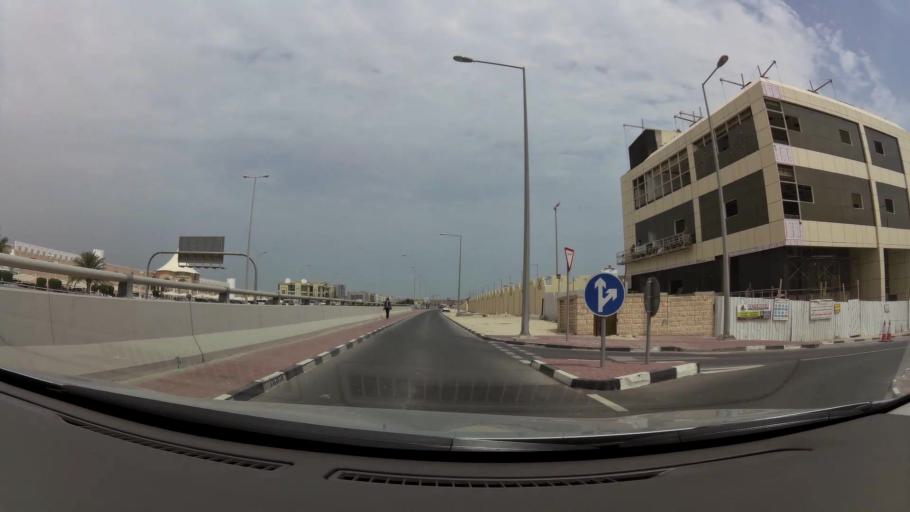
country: QA
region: Baladiyat ar Rayyan
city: Ar Rayyan
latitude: 25.3324
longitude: 51.4666
